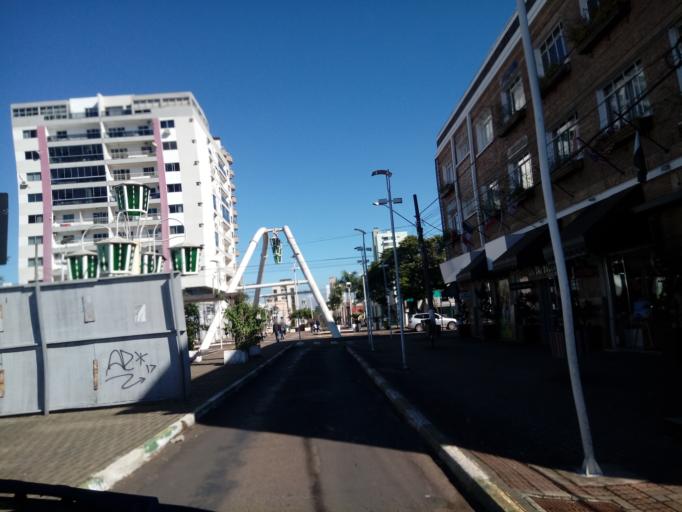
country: BR
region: Santa Catarina
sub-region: Chapeco
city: Chapeco
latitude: -27.0990
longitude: -52.6153
